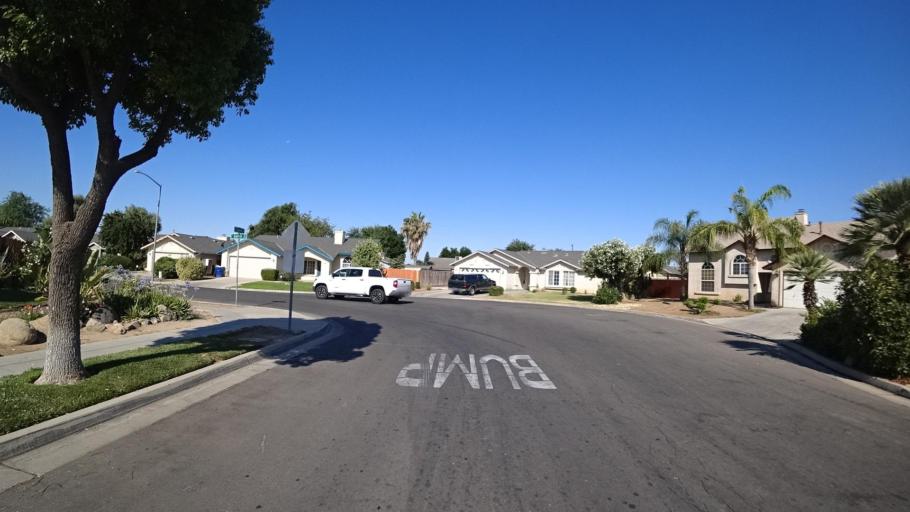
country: US
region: California
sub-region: Fresno County
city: Sunnyside
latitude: 36.7131
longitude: -119.7336
